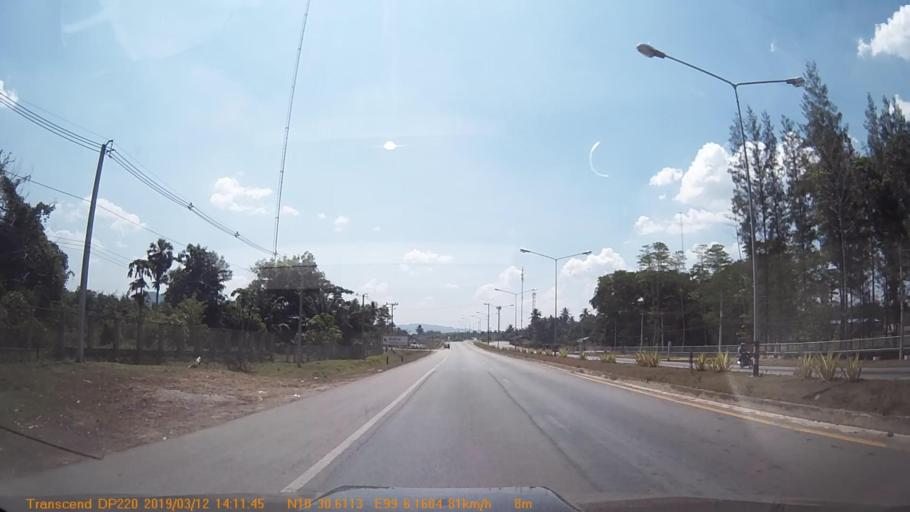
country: TH
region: Chumphon
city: Chumphon
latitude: 10.5102
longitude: 99.1026
